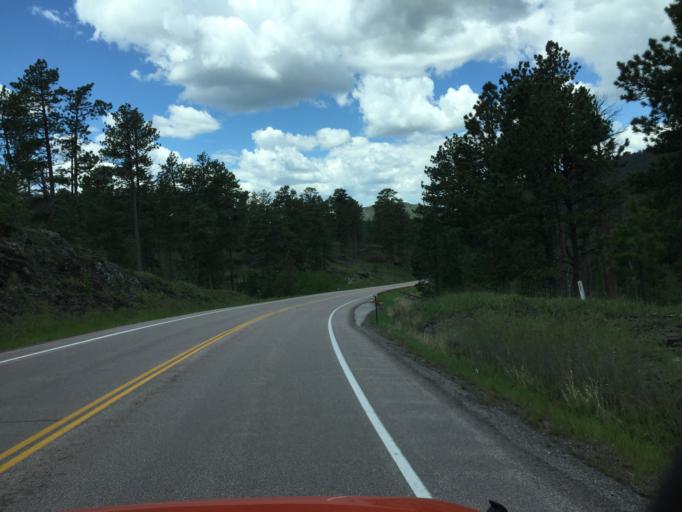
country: US
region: South Dakota
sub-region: Custer County
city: Custer
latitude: 43.9002
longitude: -103.5301
